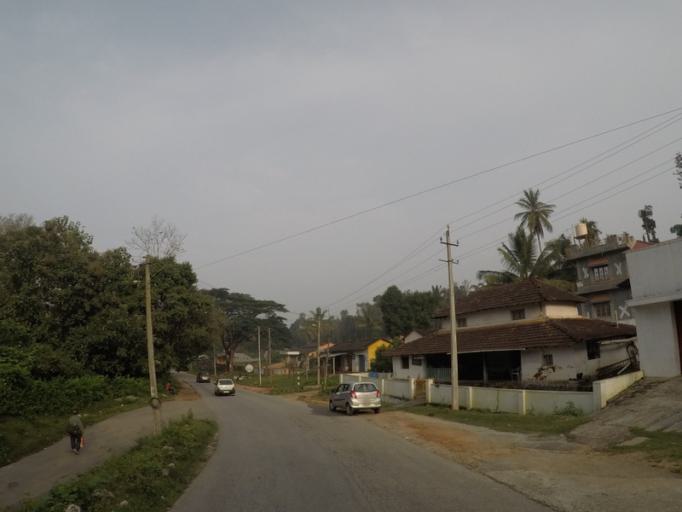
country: IN
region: Karnataka
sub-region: Chikmagalur
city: Chikmagalur
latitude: 13.2632
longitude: 75.6861
